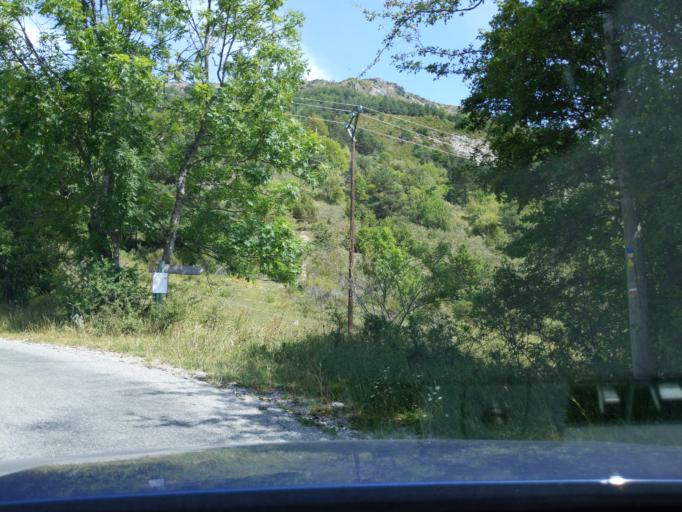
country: FR
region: Provence-Alpes-Cote d'Azur
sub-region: Departement des Hautes-Alpes
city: Veynes
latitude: 44.6332
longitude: 5.6597
